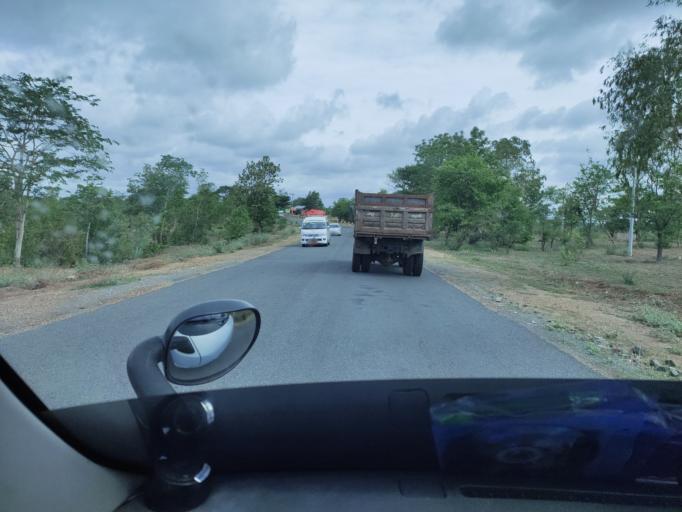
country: MM
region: Magway
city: Chauk
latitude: 20.9800
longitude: 95.0491
